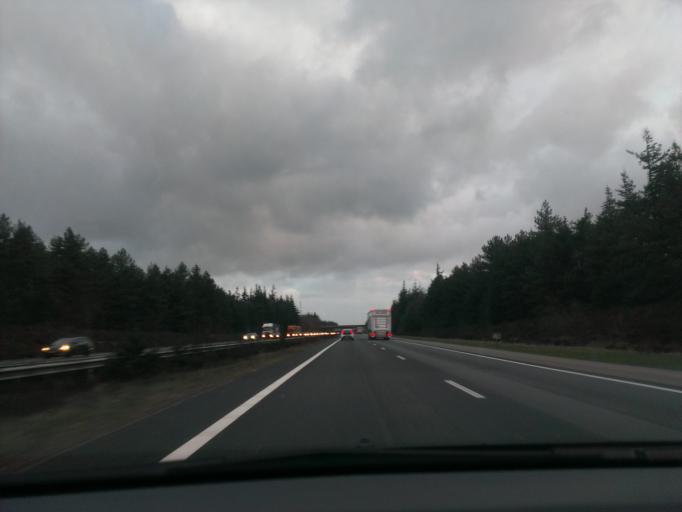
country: NL
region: Gelderland
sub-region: Gemeente Heerde
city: Heerde
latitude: 52.4212
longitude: 6.0169
